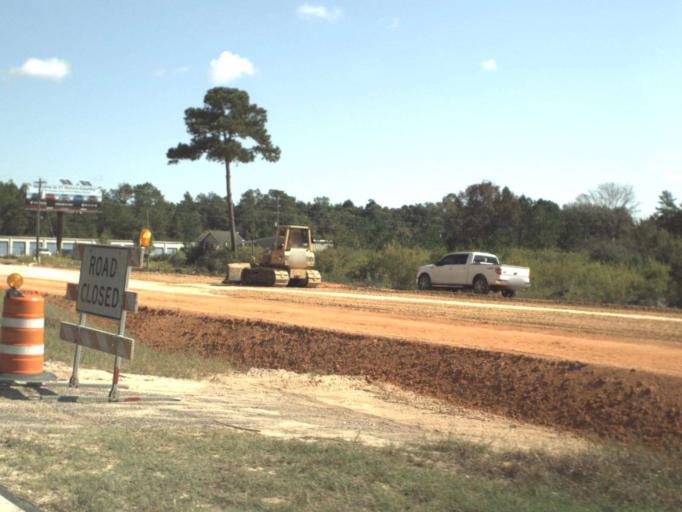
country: US
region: Florida
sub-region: Walton County
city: Freeport
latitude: 30.4765
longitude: -86.1272
